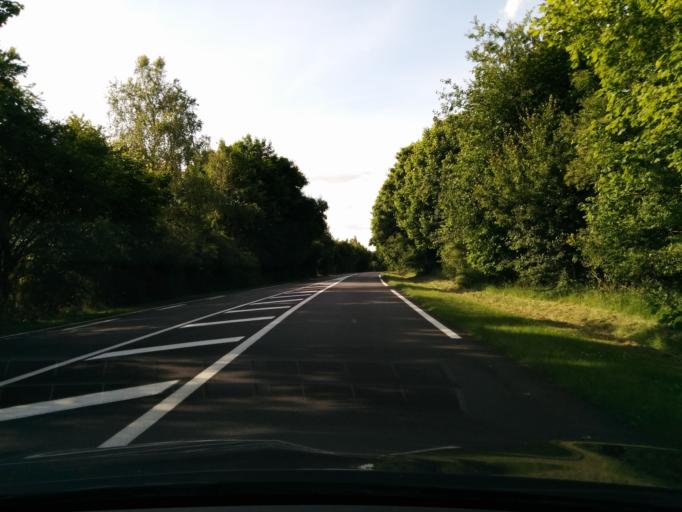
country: FR
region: Haute-Normandie
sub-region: Departement de l'Eure
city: Saint-Just
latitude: 49.1270
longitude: 1.4545
